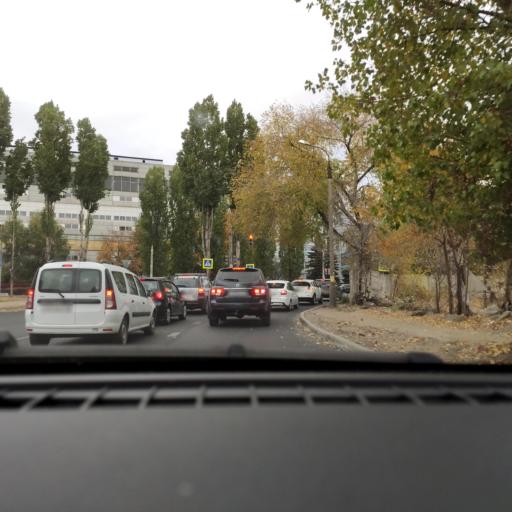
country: RU
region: Voronezj
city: Voronezh
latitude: 51.6752
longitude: 39.2570
